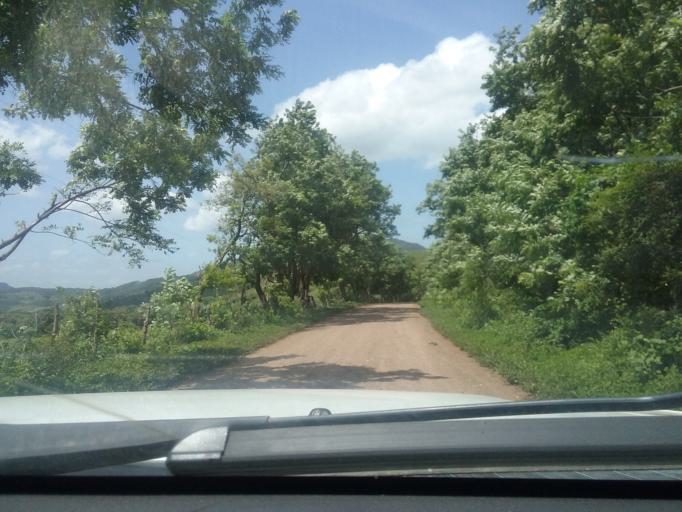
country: NI
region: Matagalpa
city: Terrabona
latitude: 12.6930
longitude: -85.9528
